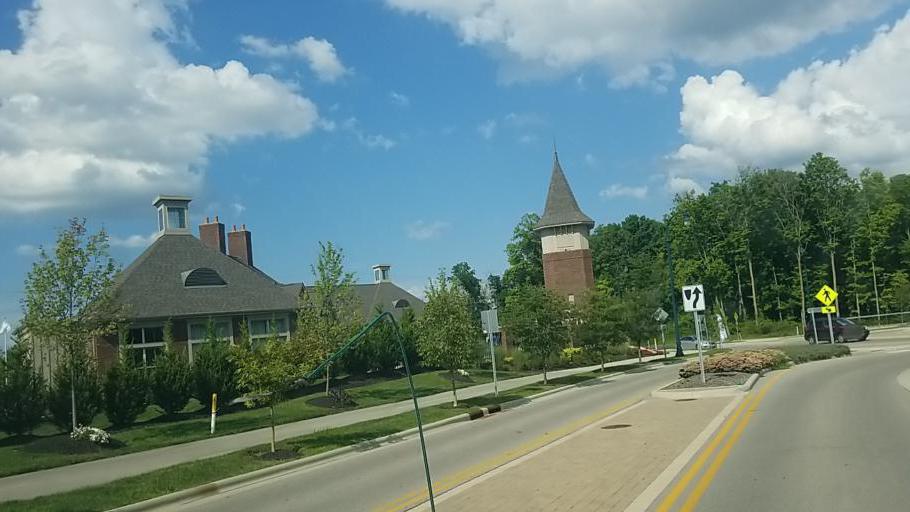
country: US
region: Ohio
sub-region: Franklin County
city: Westerville
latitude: 40.1407
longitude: -82.9572
